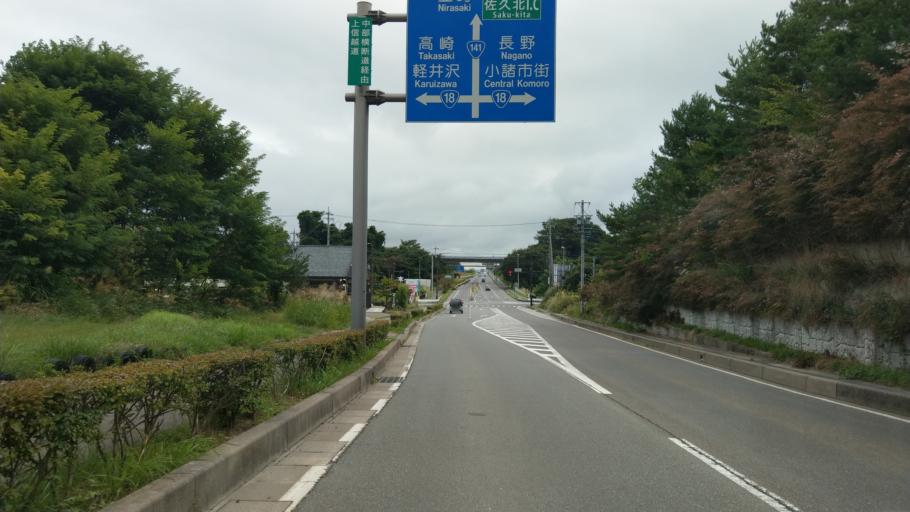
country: JP
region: Nagano
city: Komoro
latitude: 36.3149
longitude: 138.4572
